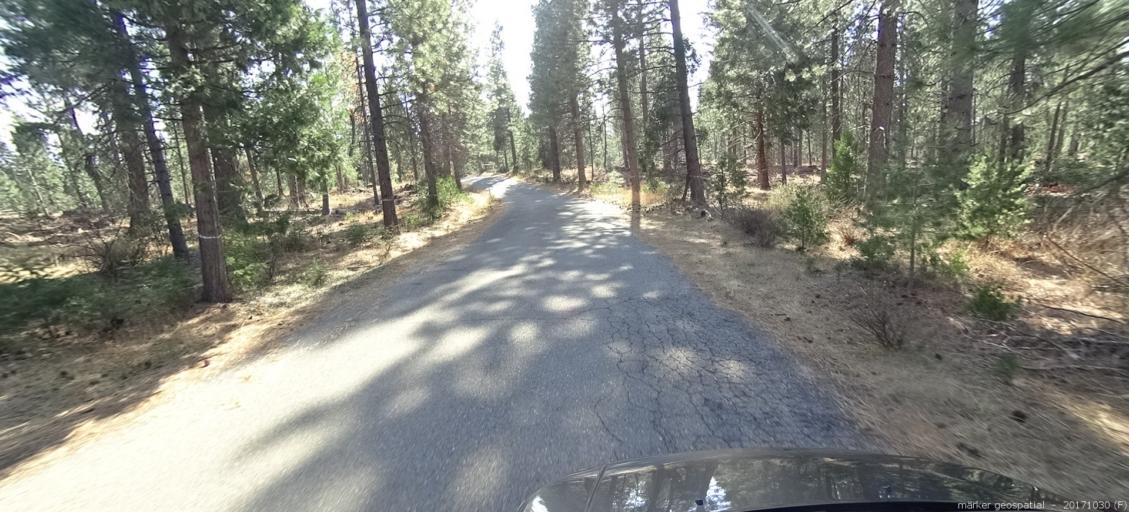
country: US
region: California
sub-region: Shasta County
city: Shingletown
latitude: 40.5156
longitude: -121.7310
